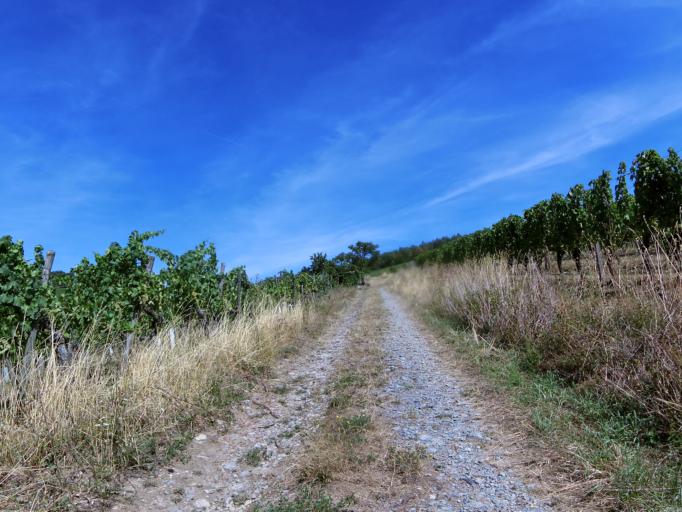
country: DE
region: Bavaria
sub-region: Regierungsbezirk Unterfranken
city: Eibelstadt
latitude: 49.7438
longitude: 9.9974
